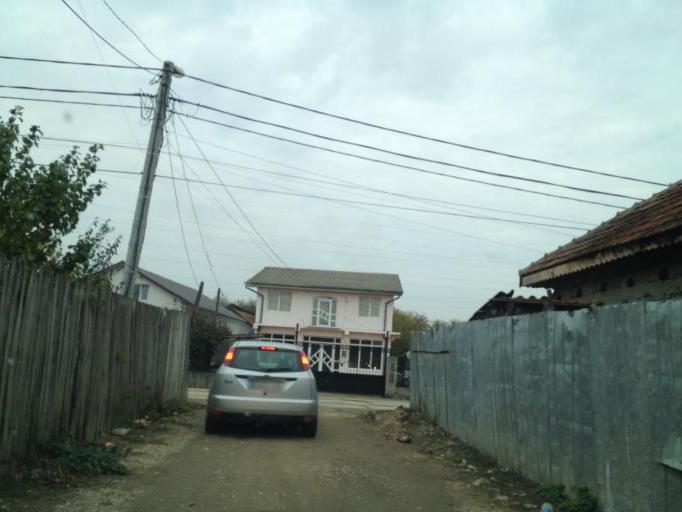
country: RO
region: Dolj
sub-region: Municipiul Craiova
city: Popoveni
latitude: 44.2980
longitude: 23.7854
